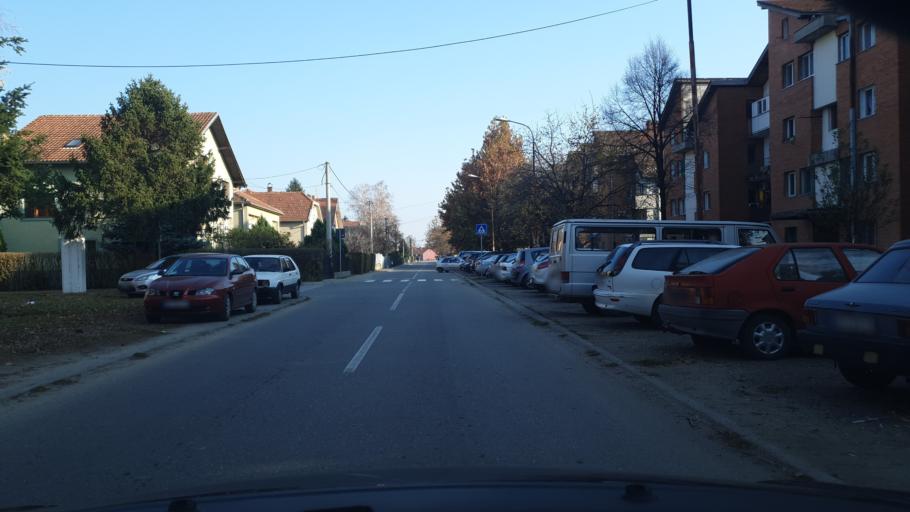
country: RS
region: Central Serbia
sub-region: Borski Okrug
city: Negotin
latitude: 44.2277
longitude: 22.5209
